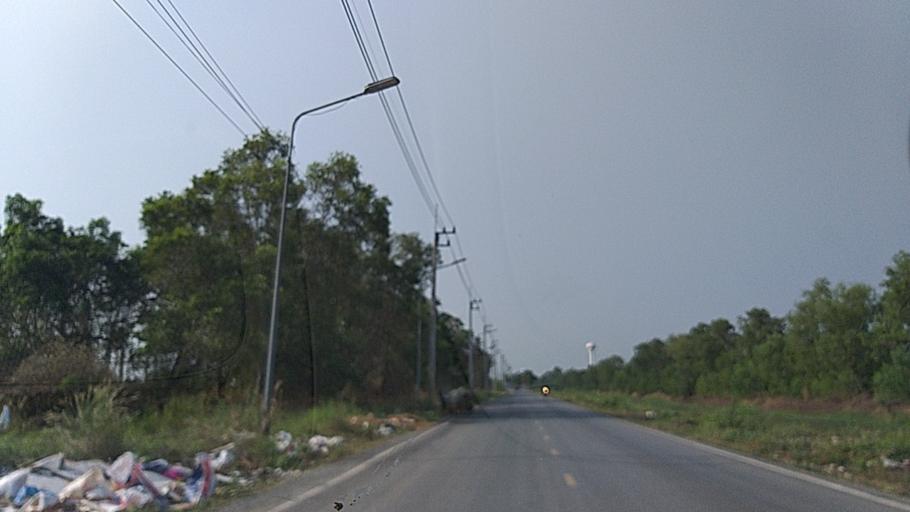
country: TH
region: Pathum Thani
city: Thanyaburi
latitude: 13.9985
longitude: 100.7071
